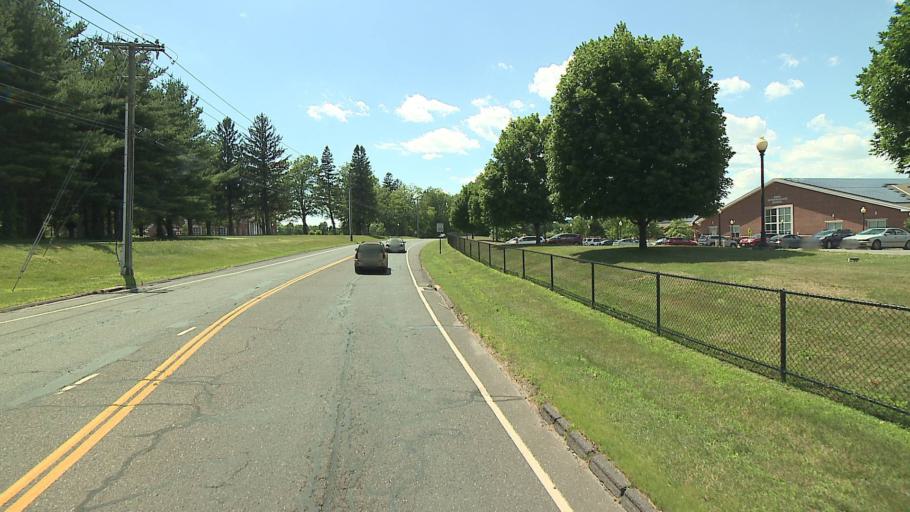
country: US
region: Connecticut
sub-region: Fairfield County
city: Newtown
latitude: 41.4032
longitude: -73.2879
